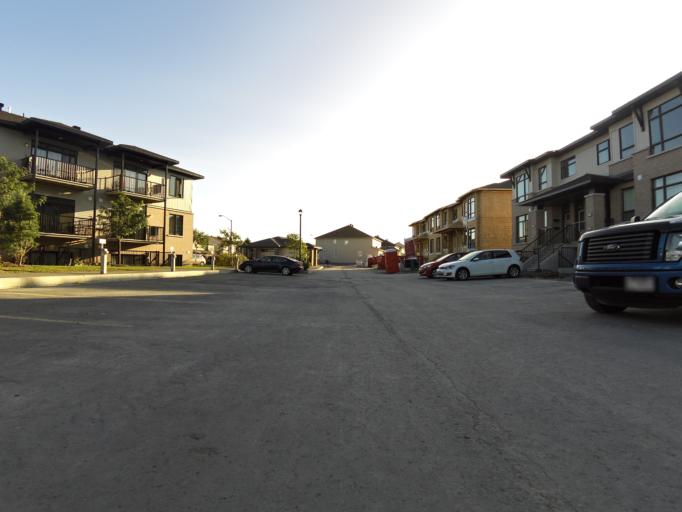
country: CA
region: Ontario
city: Bells Corners
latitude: 45.2870
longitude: -75.7316
